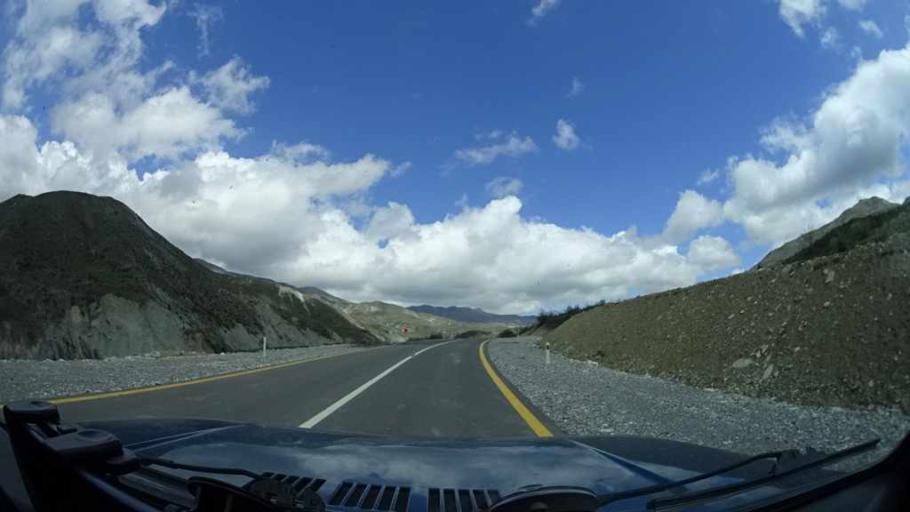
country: AZ
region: Ismayilli
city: Basqal
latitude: 40.8781
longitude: 48.4196
